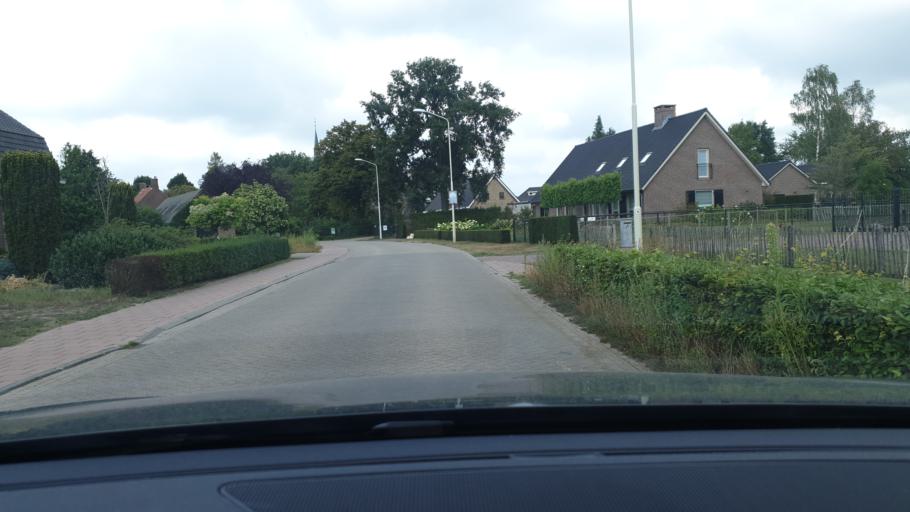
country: NL
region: North Brabant
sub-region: Gemeente Oirschot
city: Oostelbeers
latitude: 51.4692
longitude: 5.2733
